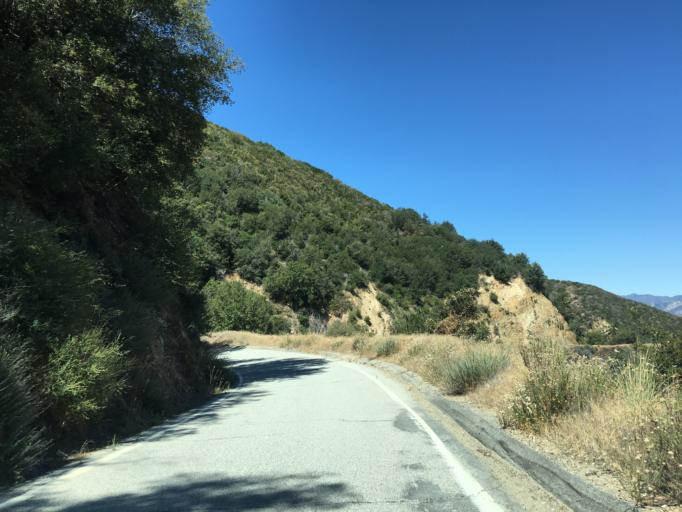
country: US
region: California
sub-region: San Bernardino County
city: San Antonio Heights
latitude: 34.2235
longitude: -117.7244
